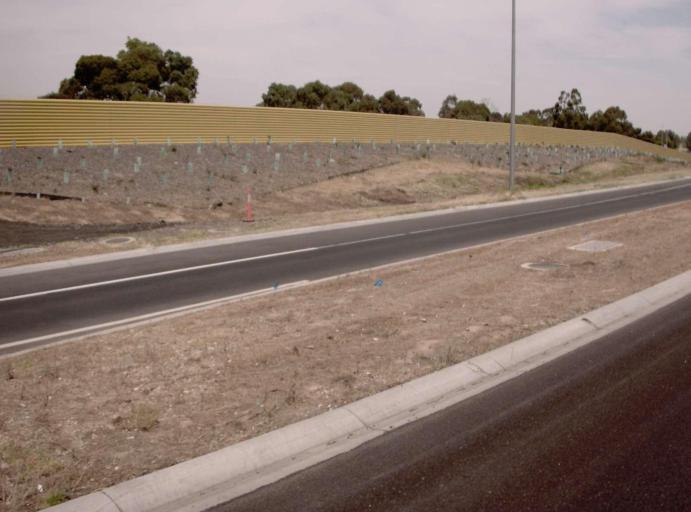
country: AU
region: Victoria
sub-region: Brimbank
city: Sunshine North
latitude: -37.7588
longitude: 144.8223
